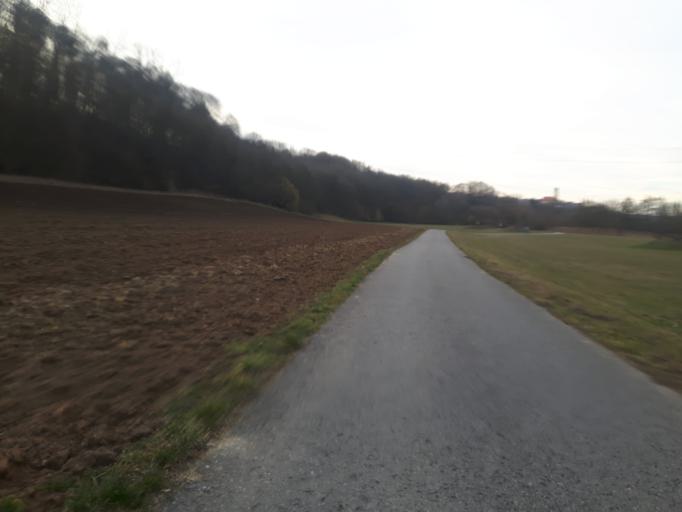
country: DE
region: Baden-Wuerttemberg
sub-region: Regierungsbezirk Stuttgart
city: Neuenstadt am Kocher
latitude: 49.2446
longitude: 9.2996
